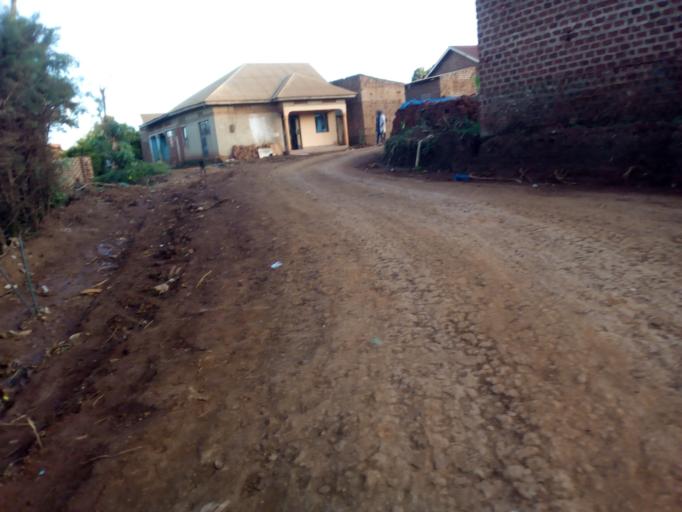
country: UG
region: Central Region
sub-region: Kampala District
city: Kampala
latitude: 0.2496
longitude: 32.5759
